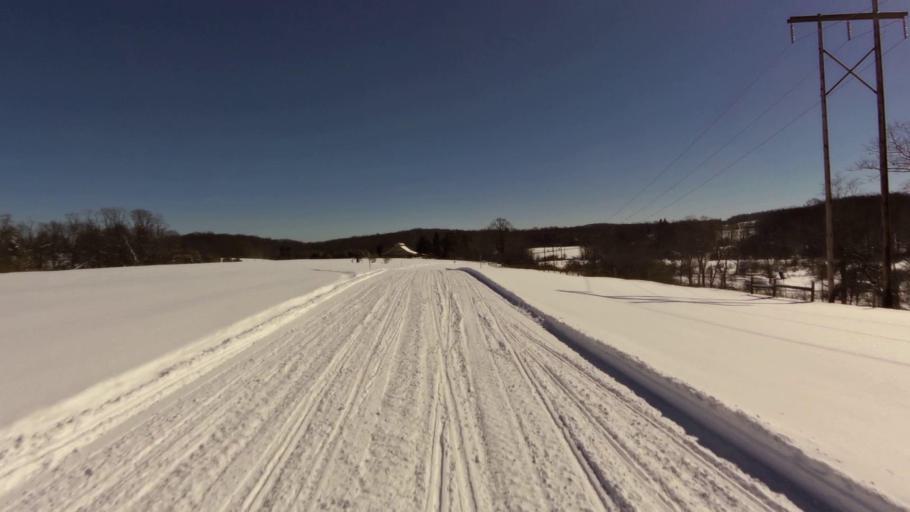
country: US
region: New York
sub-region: Chautauqua County
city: Mayville
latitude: 42.2275
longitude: -79.5198
